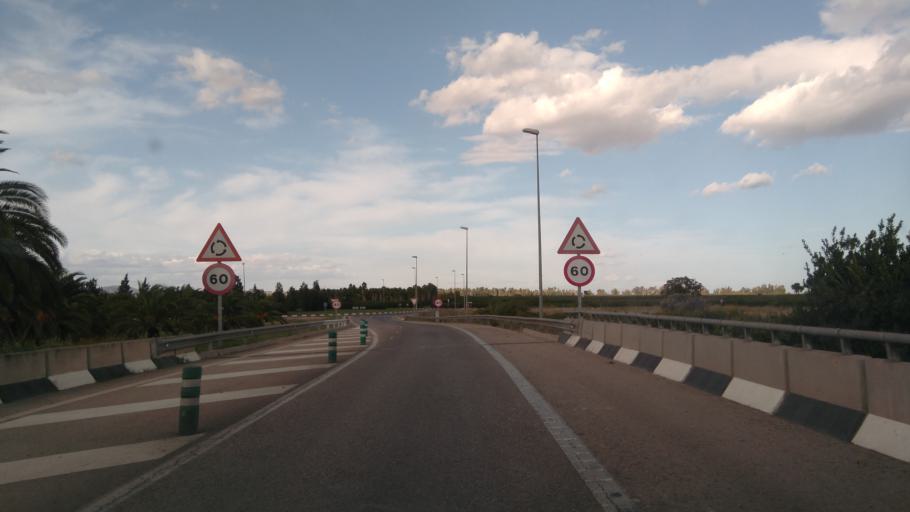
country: ES
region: Valencia
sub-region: Provincia de Valencia
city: L'Alcudia
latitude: 39.1911
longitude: -0.4933
